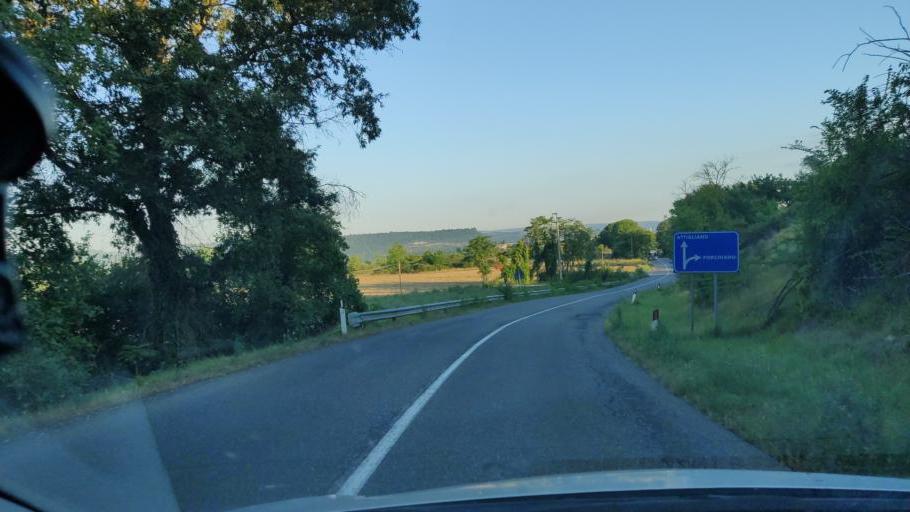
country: IT
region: Umbria
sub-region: Provincia di Terni
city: Attigliano
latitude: 42.5058
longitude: 12.3089
